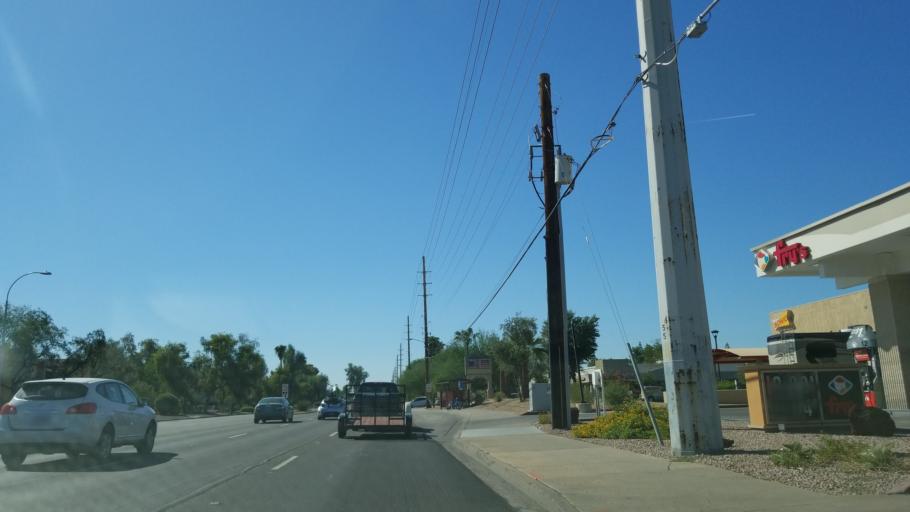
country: US
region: Arizona
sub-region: Maricopa County
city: Scottsdale
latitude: 33.4809
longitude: -111.9091
